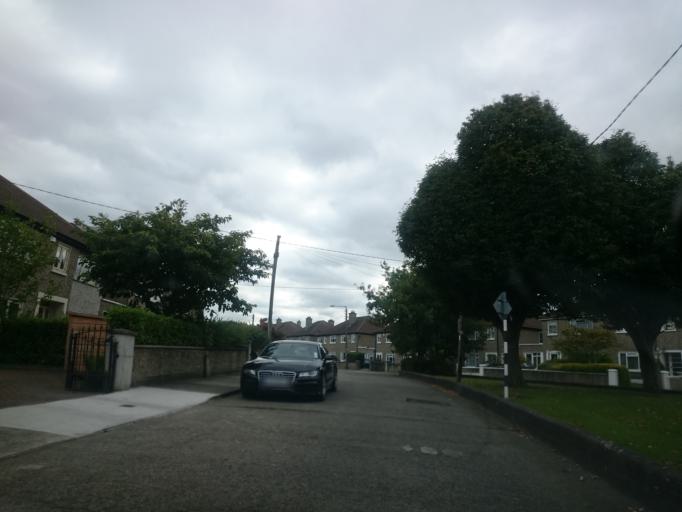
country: IE
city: Booterstown
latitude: 53.3097
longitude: -6.2046
